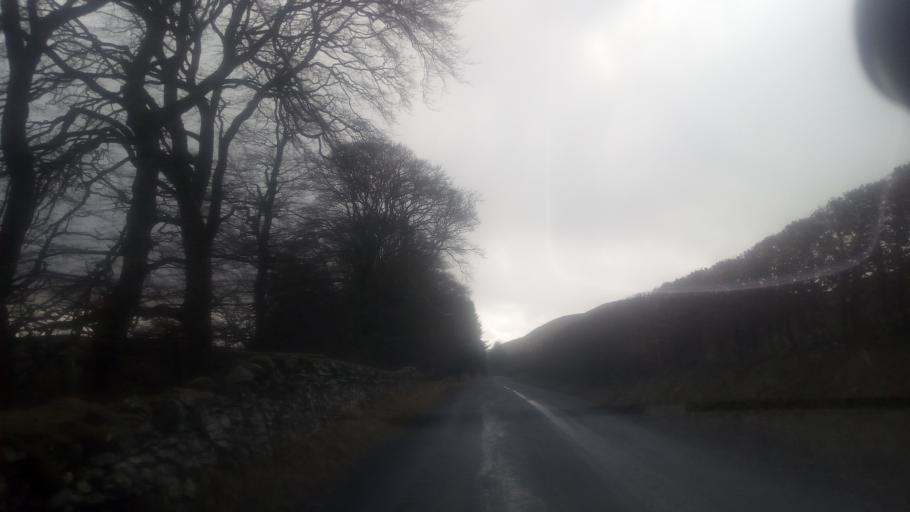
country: GB
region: Scotland
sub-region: The Scottish Borders
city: Innerleithen
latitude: 55.4543
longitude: -3.1004
